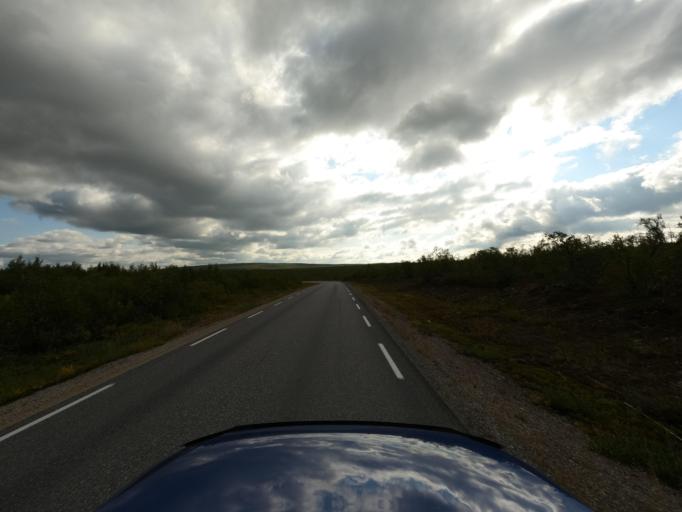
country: NO
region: Finnmark Fylke
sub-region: Porsanger
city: Lakselv
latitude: 69.3694
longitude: 24.2827
